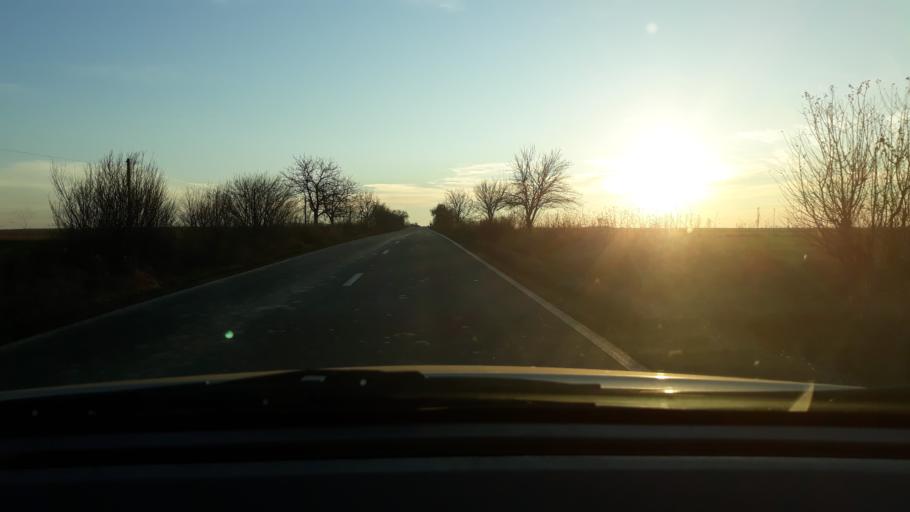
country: RO
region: Bihor
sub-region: Comuna Spinus
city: Spinus
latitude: 47.2458
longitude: 22.2016
